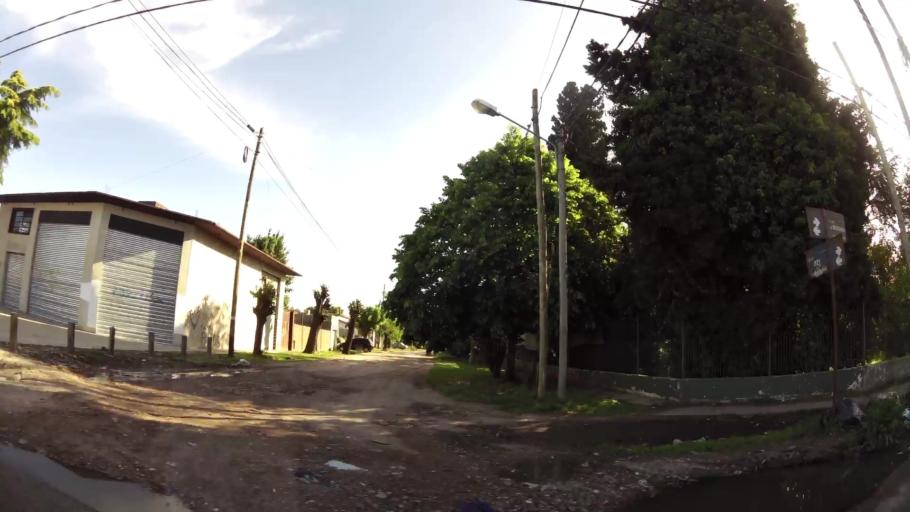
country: AR
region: Buenos Aires
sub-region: Partido de Quilmes
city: Quilmes
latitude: -34.8087
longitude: -58.2113
